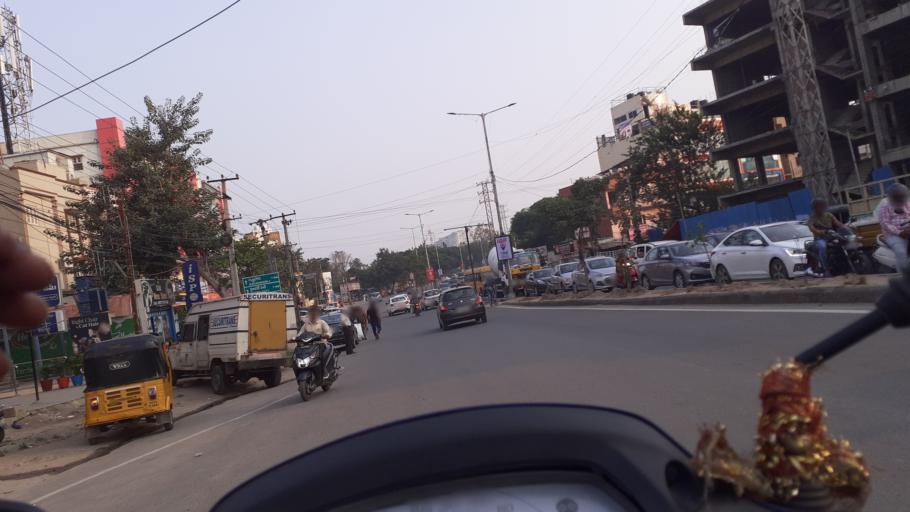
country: IN
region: Telangana
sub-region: Medak
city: Serilingampalle
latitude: 17.4932
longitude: 78.3519
